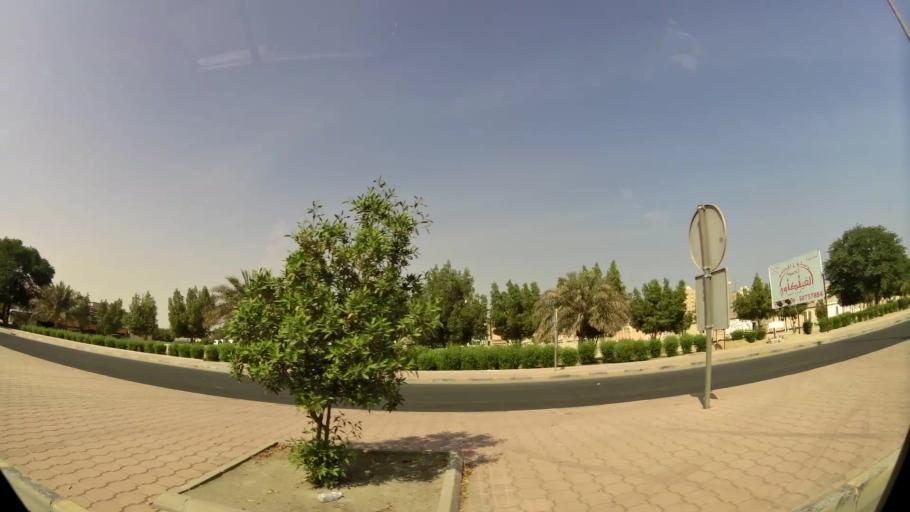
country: KW
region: Al Ahmadi
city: Al Manqaf
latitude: 29.0914
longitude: 48.1241
